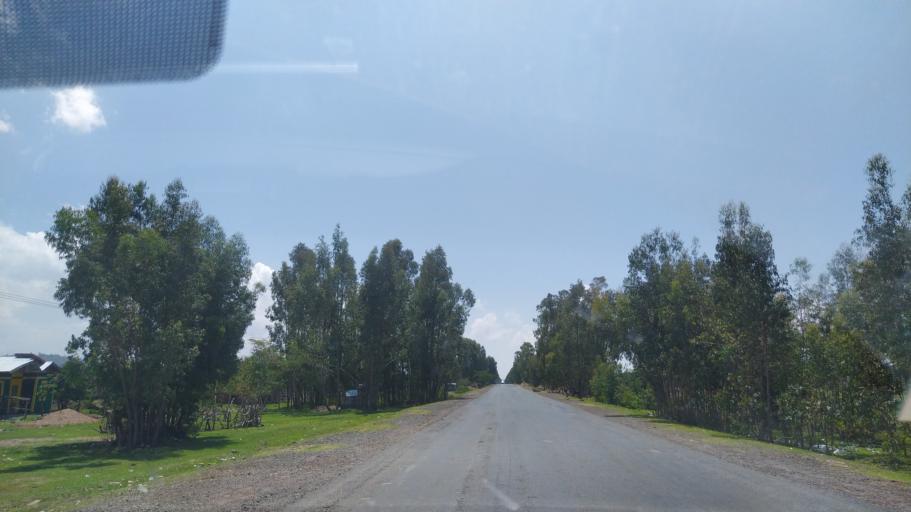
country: ET
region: Southern Nations, Nationalities, and People's Region
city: Butajira
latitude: 7.7889
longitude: 38.1450
